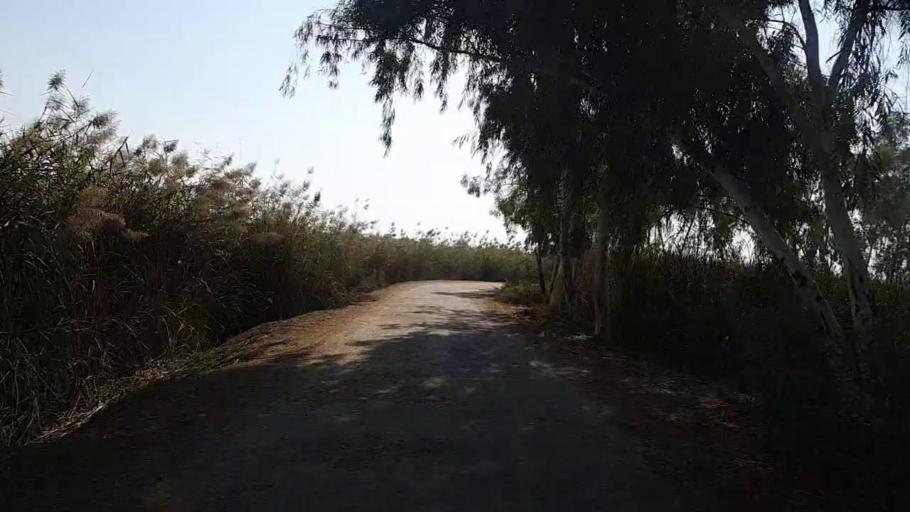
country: PK
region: Sindh
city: Bozdar
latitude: 27.1926
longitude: 68.6389
